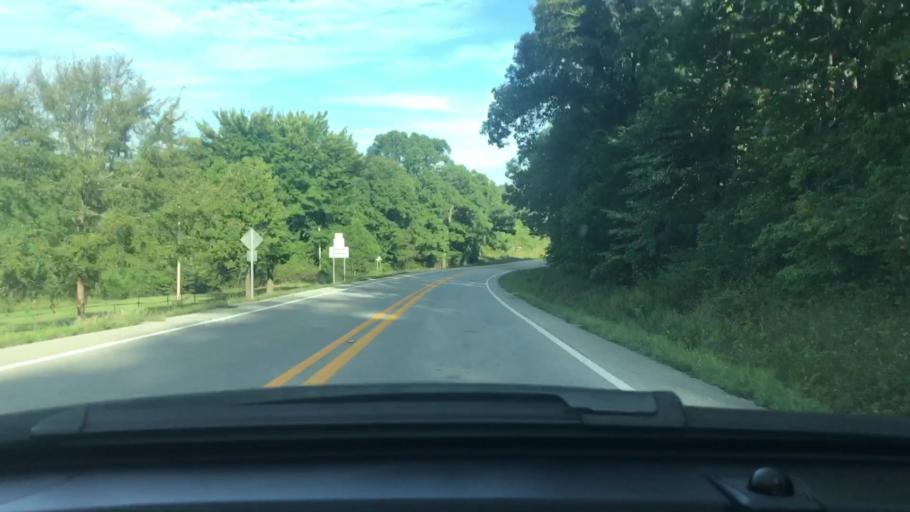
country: US
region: Arkansas
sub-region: Sharp County
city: Cherokee Village
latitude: 36.2741
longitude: -91.3395
